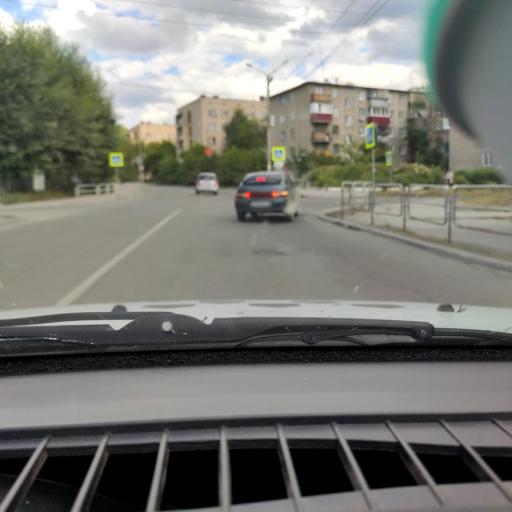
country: RU
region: Chelyabinsk
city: Miass
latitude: 55.0636
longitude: 60.1132
